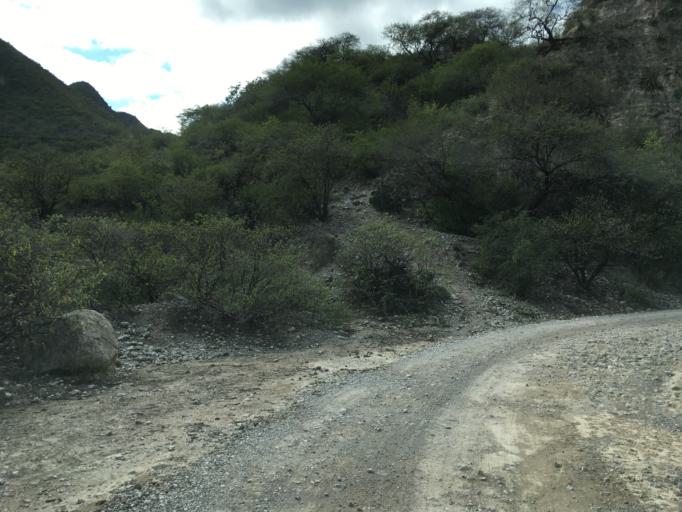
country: MX
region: Hidalgo
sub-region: Metztitlan
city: Fontezuelas
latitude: 20.6379
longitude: -98.9279
